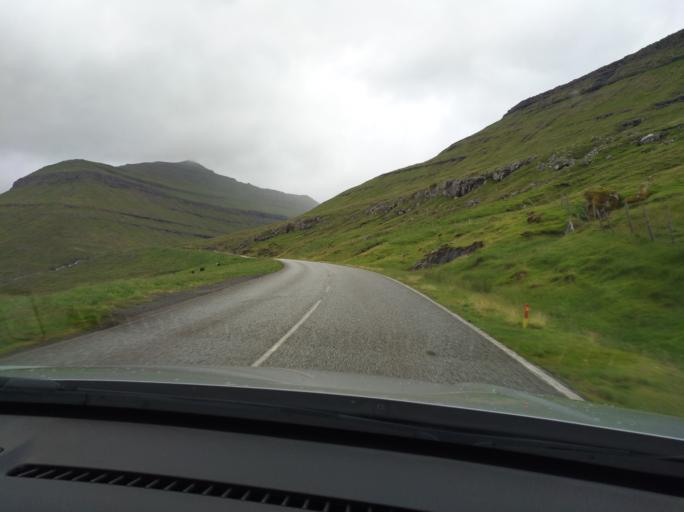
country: FO
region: Eysturoy
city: Fuglafjordur
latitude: 62.2165
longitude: -6.8639
